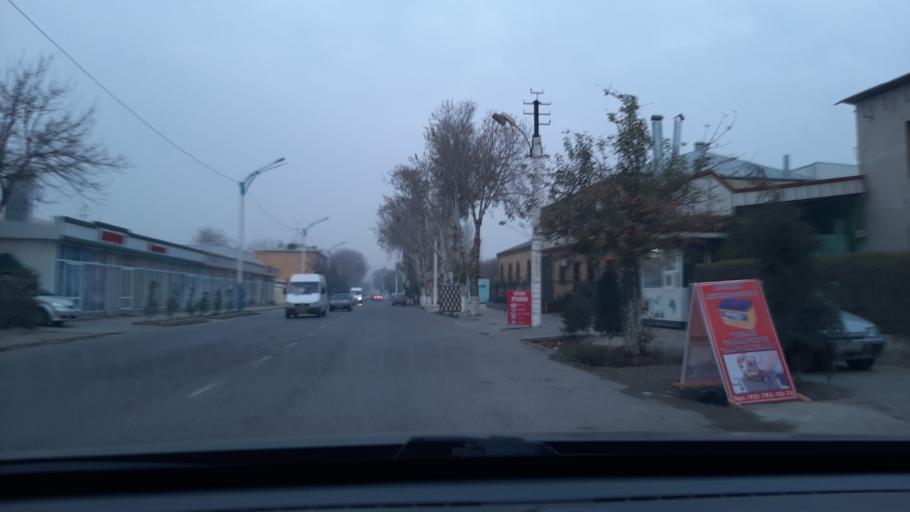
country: TJ
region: Viloyati Sughd
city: Khujand
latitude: 40.2701
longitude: 69.6035
